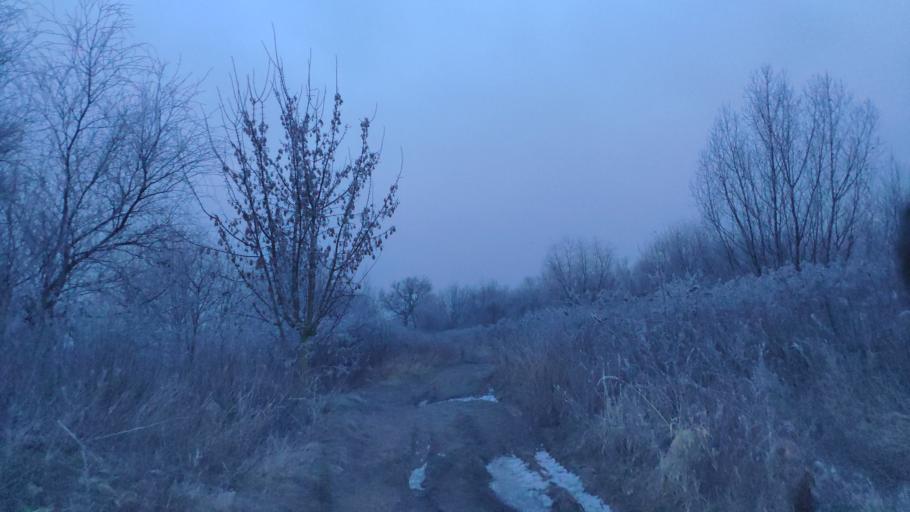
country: SK
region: Kosicky
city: Kosice
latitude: 48.6140
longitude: 21.3352
